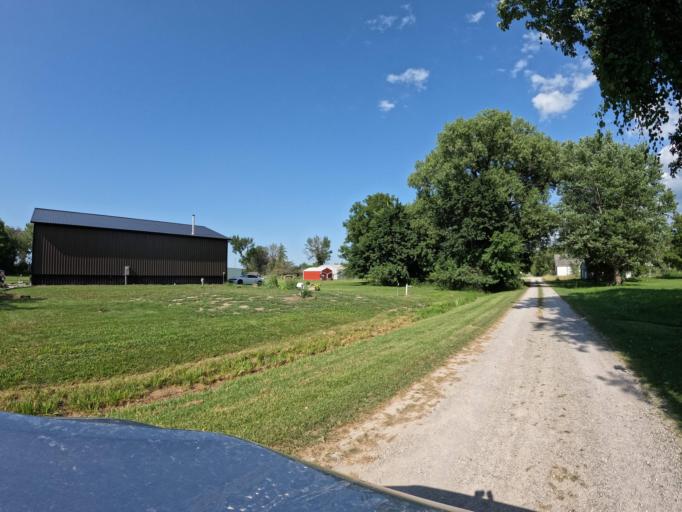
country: US
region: Iowa
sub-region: Appanoose County
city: Centerville
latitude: 40.7187
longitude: -93.0316
